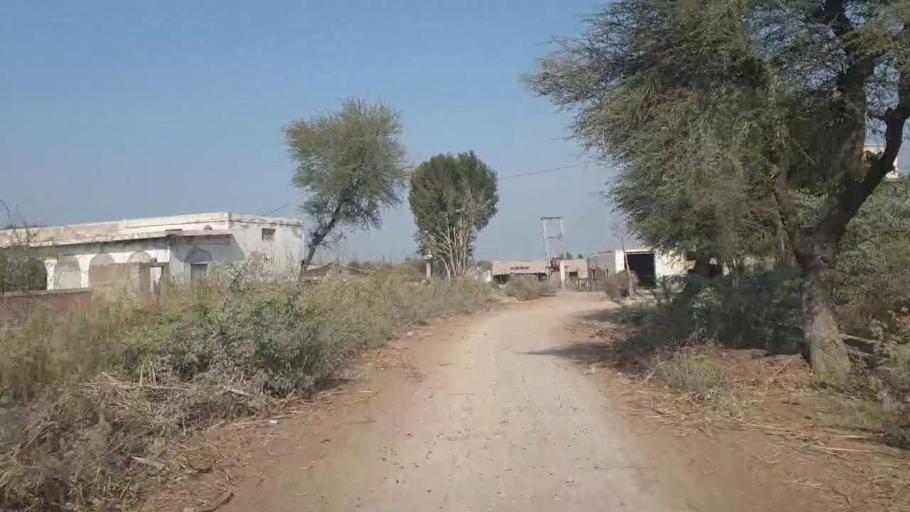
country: PK
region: Sindh
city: Tando Allahyar
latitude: 25.4499
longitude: 68.8230
